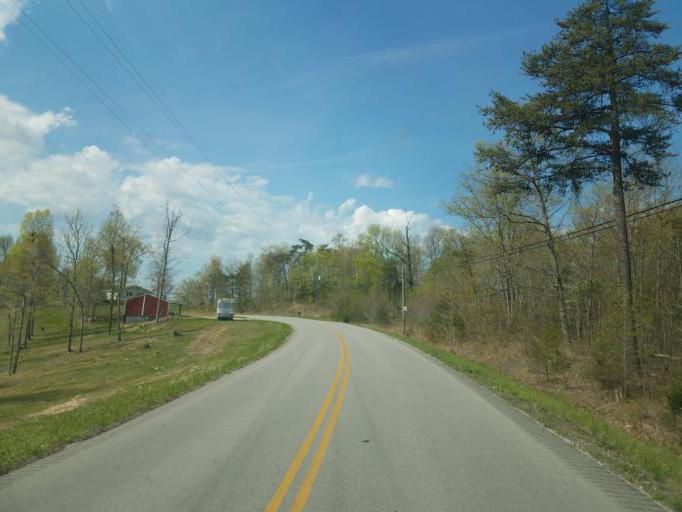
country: US
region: Kentucky
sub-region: Edmonson County
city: Brownsville
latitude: 37.2722
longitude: -86.2201
